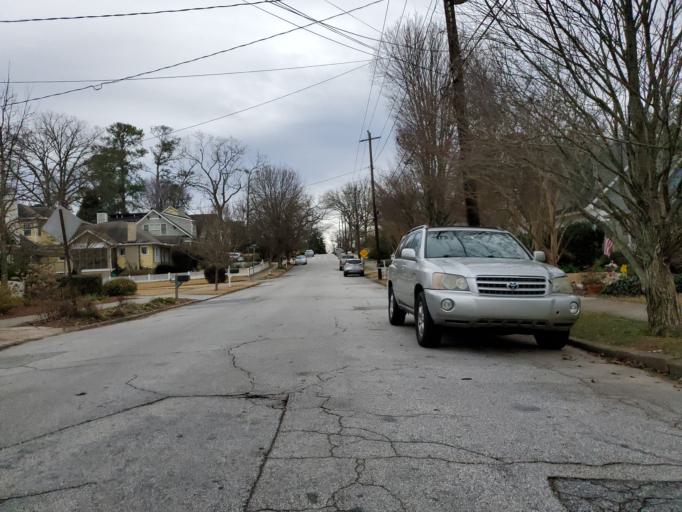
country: US
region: Georgia
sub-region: DeKalb County
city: North Decatur
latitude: 33.7854
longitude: -84.2990
